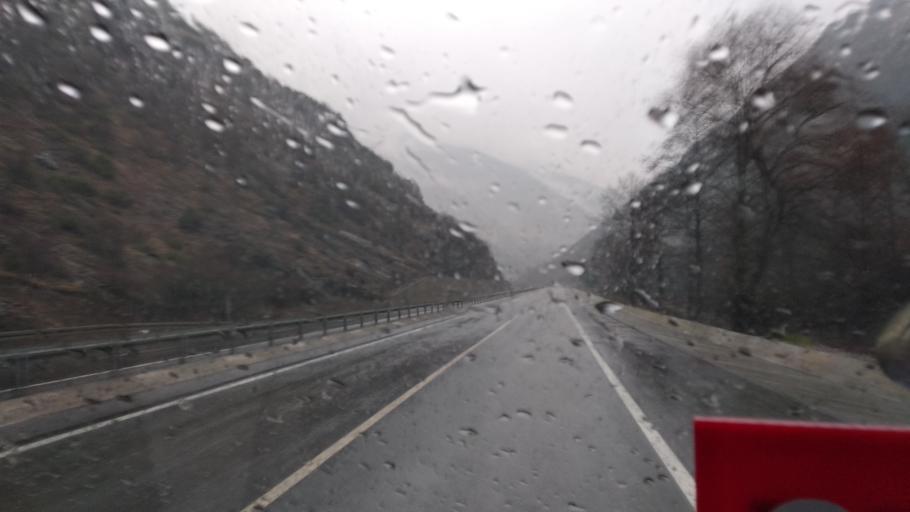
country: TR
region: Trabzon
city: Macka
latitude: 40.7922
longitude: 39.5815
